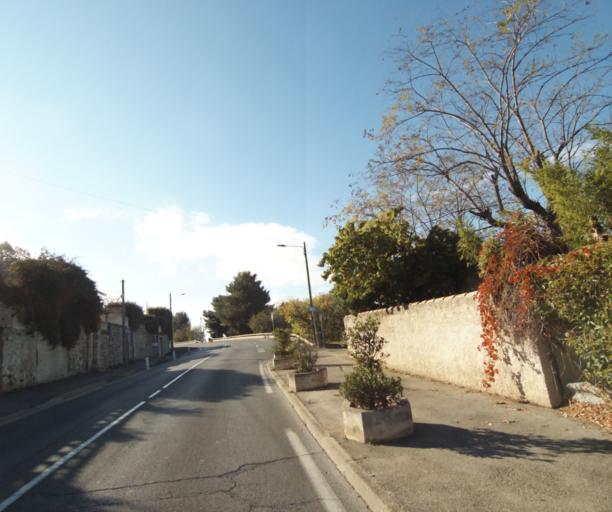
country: FR
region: Provence-Alpes-Cote d'Azur
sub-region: Departement des Bouches-du-Rhone
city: Allauch
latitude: 43.3447
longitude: 5.4867
